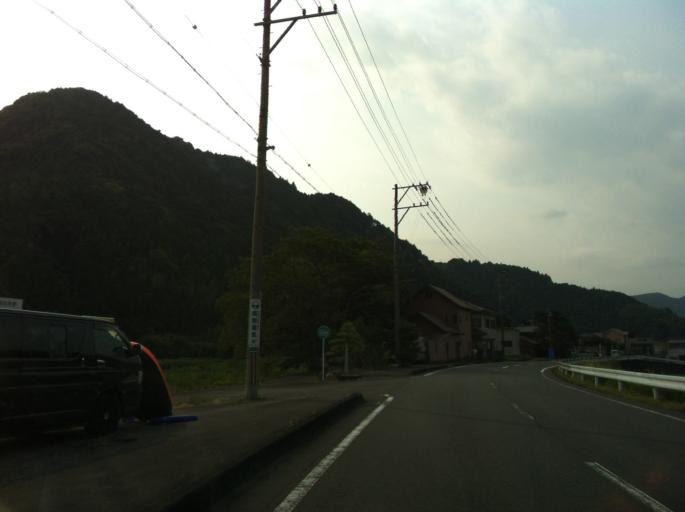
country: JP
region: Shizuoka
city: Fujieda
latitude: 34.9367
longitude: 138.2613
